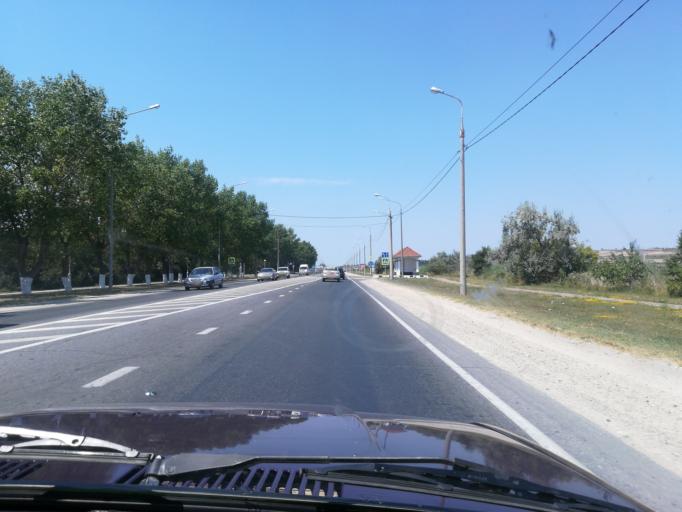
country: RU
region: Krasnodarskiy
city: Anapa
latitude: 44.9321
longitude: 37.3221
